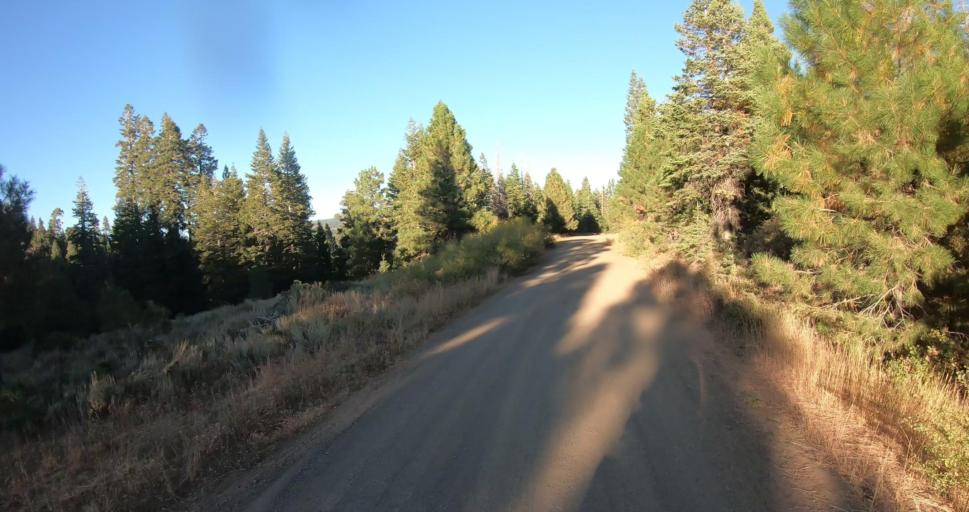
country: US
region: Oregon
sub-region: Lake County
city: Lakeview
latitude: 42.2105
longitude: -120.2903
